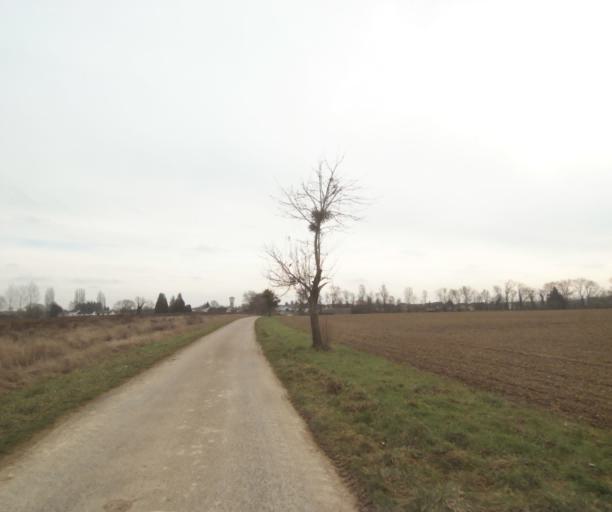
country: FR
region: Champagne-Ardenne
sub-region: Departement de la Haute-Marne
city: Villiers-en-Lieu
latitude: 48.6708
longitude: 4.8889
